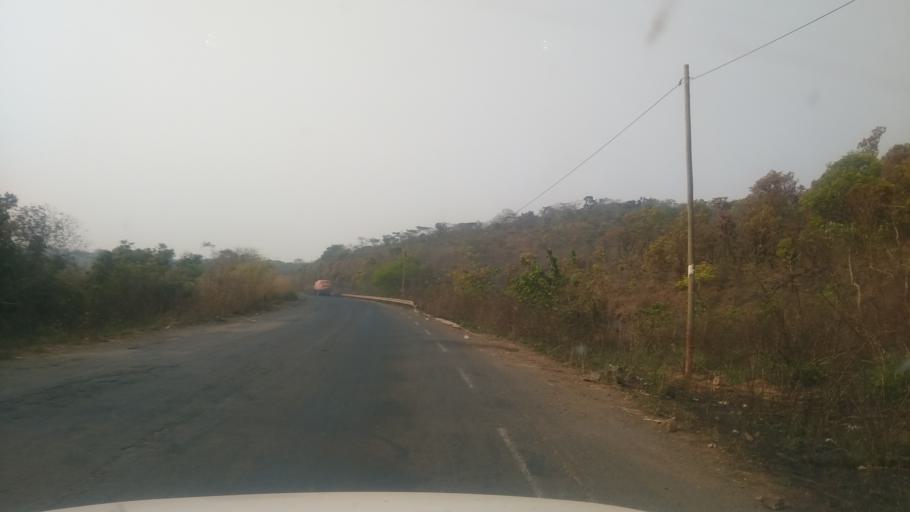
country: CM
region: West
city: Tonga
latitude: 5.0414
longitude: 10.7018
